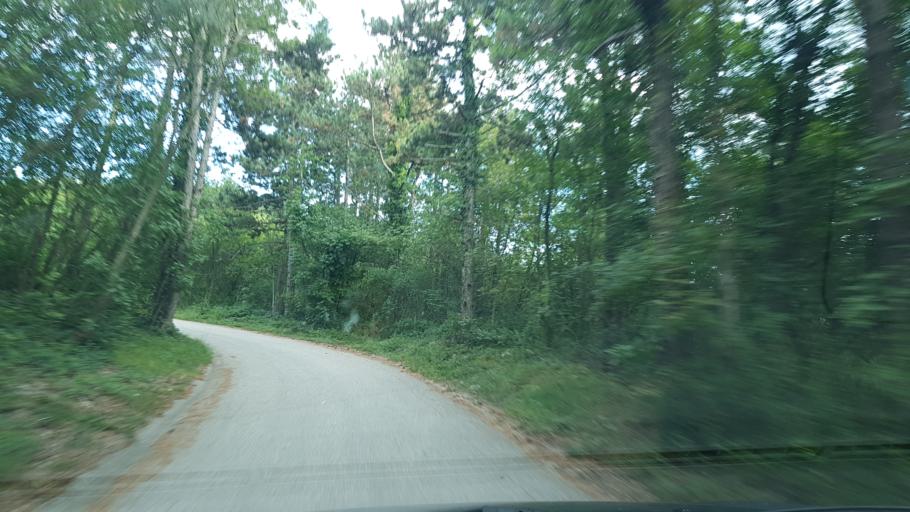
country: SI
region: Rence-Vogrsko
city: Rence
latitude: 45.8553
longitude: 13.6874
